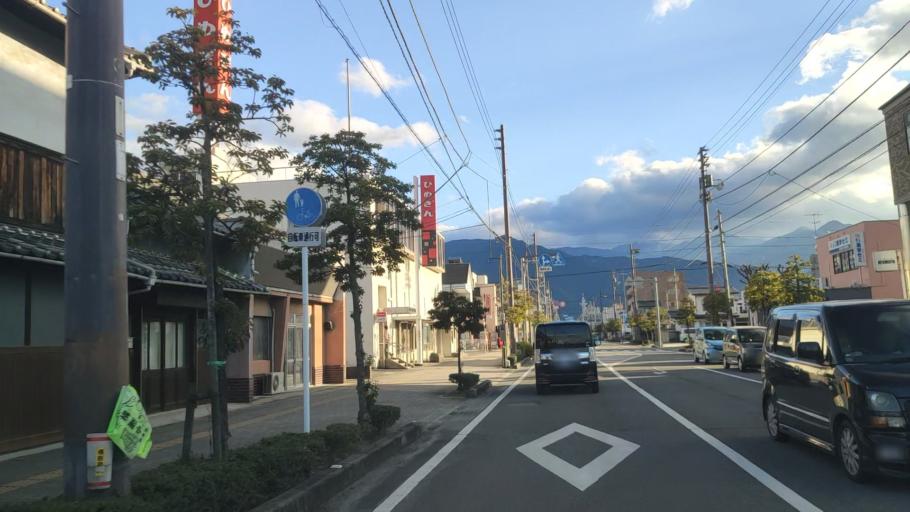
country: JP
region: Ehime
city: Saijo
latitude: 33.9180
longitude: 133.1857
